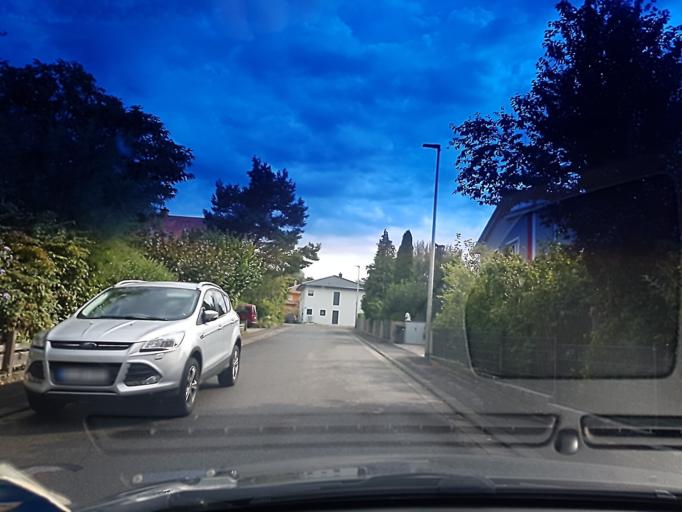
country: DE
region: Bavaria
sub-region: Upper Franconia
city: Frensdorf
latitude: 49.8166
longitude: 10.8602
